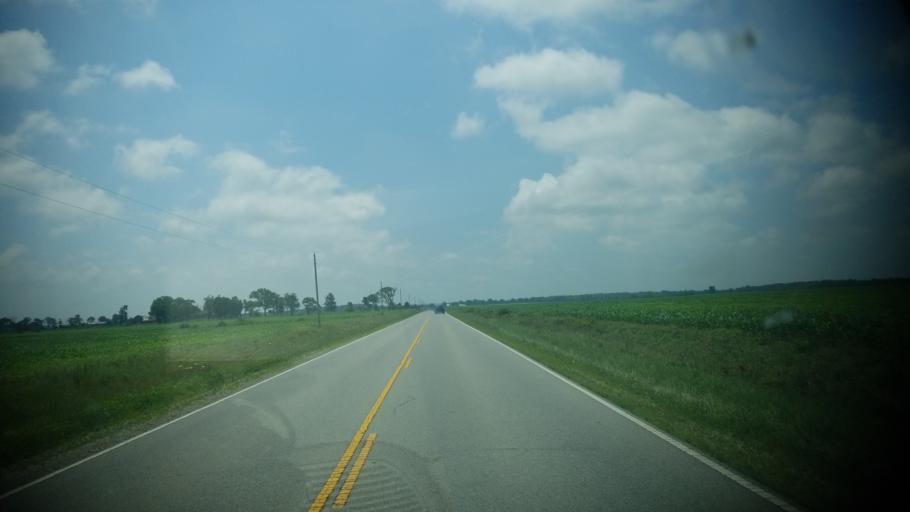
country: US
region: Illinois
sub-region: Wayne County
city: Fairfield
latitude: 38.4996
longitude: -88.3485
